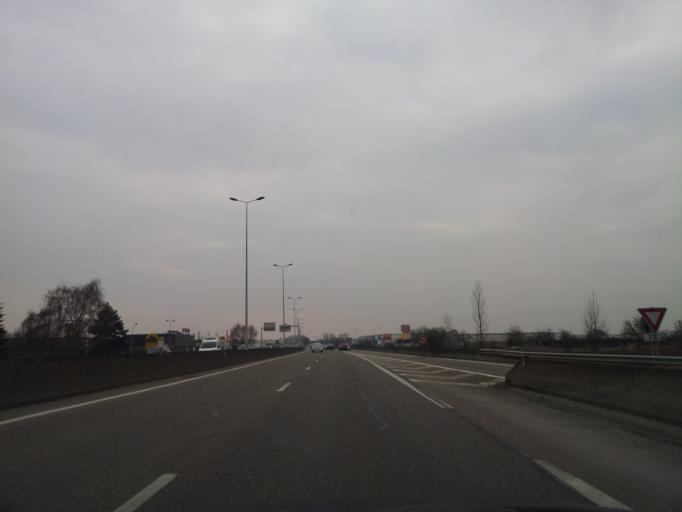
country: FR
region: Alsace
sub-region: Departement du Bas-Rhin
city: Fegersheim
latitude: 48.5050
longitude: 7.6949
